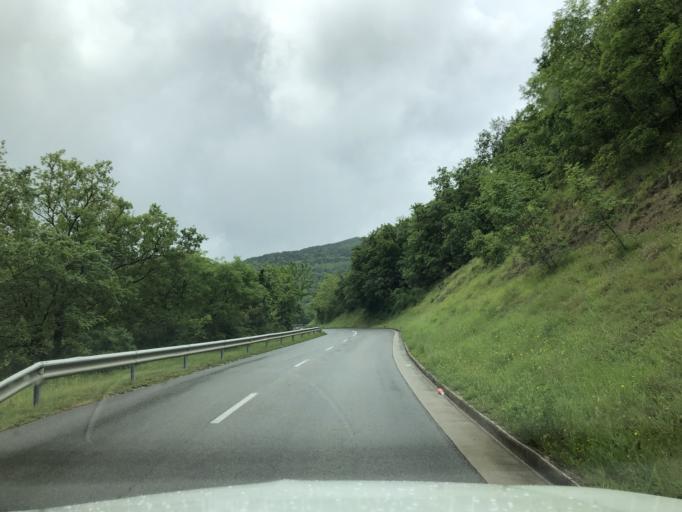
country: SI
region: Koper-Capodistria
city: Prade
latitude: 45.5077
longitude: 13.7755
